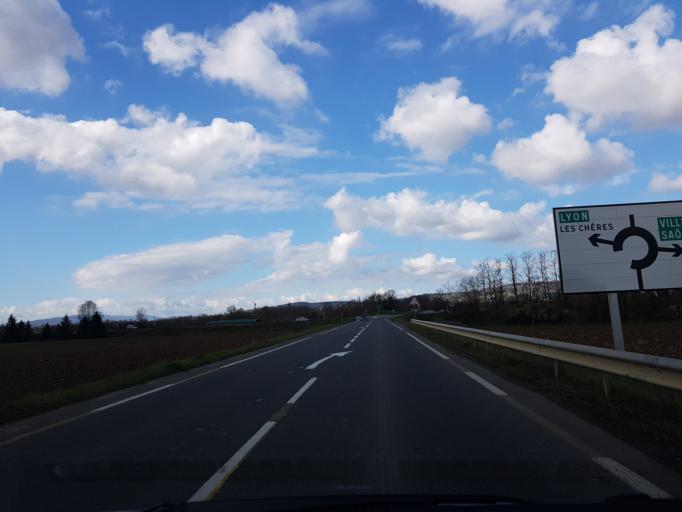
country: FR
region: Rhone-Alpes
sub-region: Departement du Rhone
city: Les Cheres
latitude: 45.9110
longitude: 4.7362
